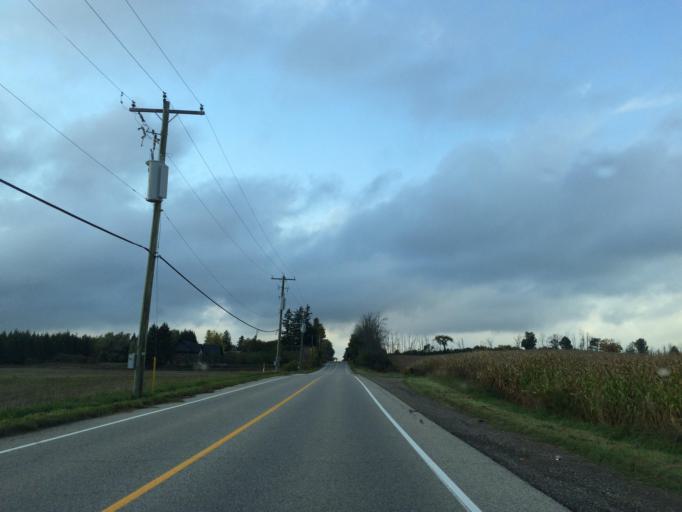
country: CA
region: Ontario
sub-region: Wellington County
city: Guelph
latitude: 43.5001
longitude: -80.2613
